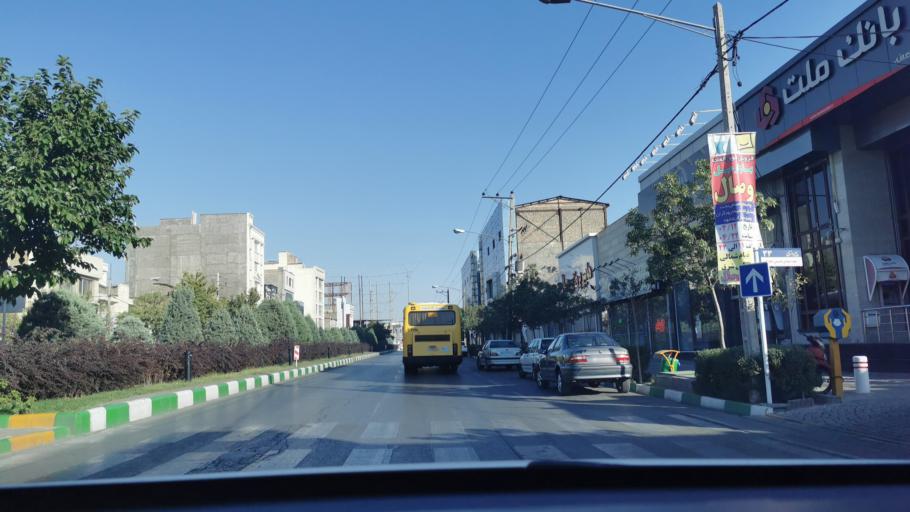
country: IR
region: Razavi Khorasan
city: Mashhad
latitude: 36.3058
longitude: 59.5108
